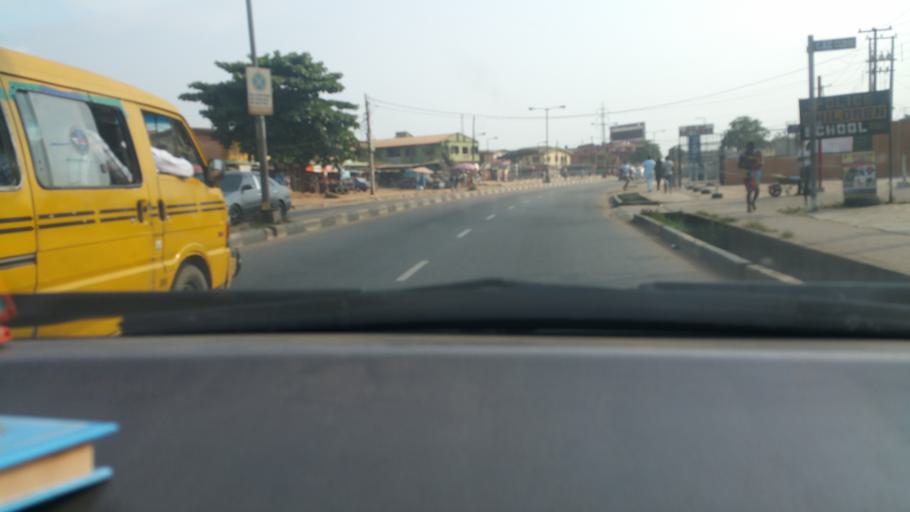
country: NG
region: Lagos
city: Ikotun
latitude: 6.5805
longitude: 3.2838
